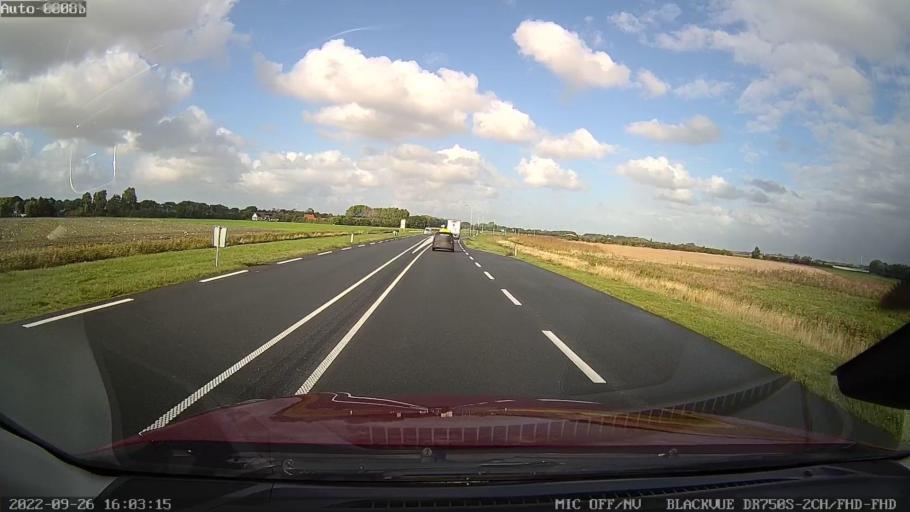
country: NL
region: Zeeland
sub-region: Schouwen-Duiveland
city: Burgh
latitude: 51.6737
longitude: 3.7280
